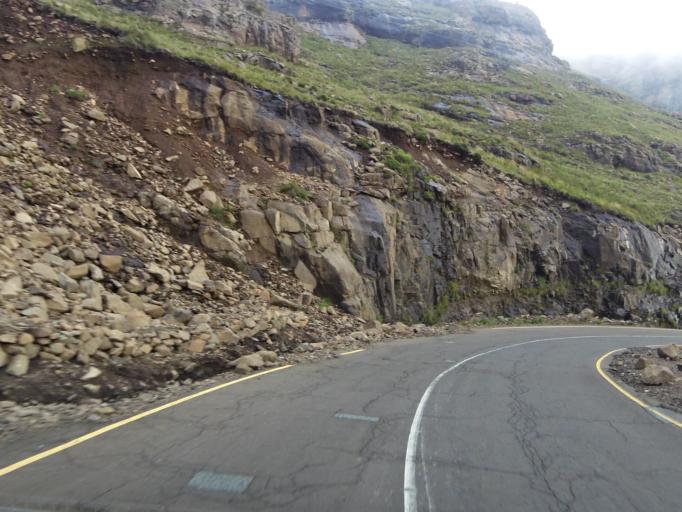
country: LS
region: Butha-Buthe
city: Butha-Buthe
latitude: -29.0633
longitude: 28.4030
